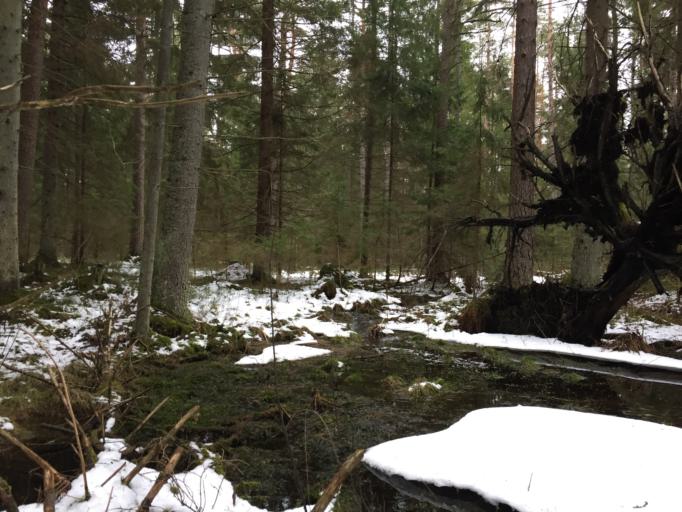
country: LV
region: Garkalne
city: Garkalne
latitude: 56.9563
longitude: 24.4651
